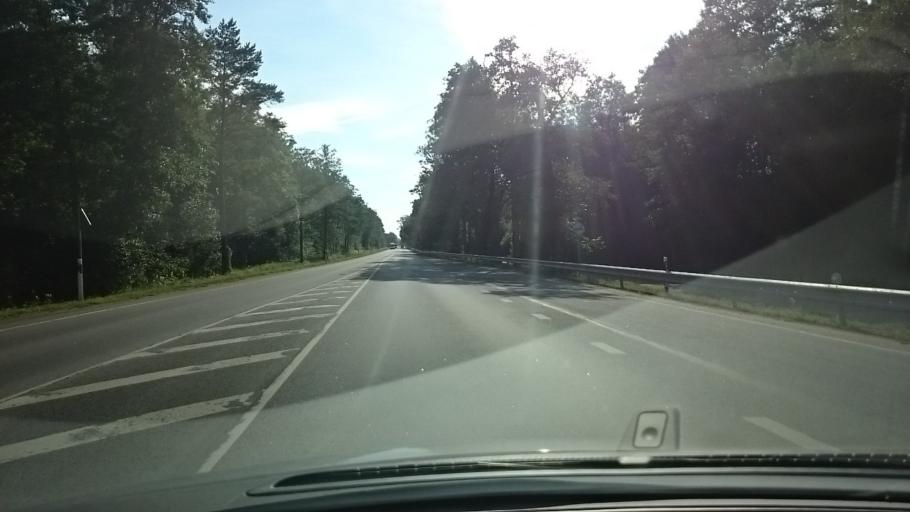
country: EE
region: Laeaene
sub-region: Ridala Parish
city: Uuemoisa
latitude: 58.9461
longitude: 23.6023
